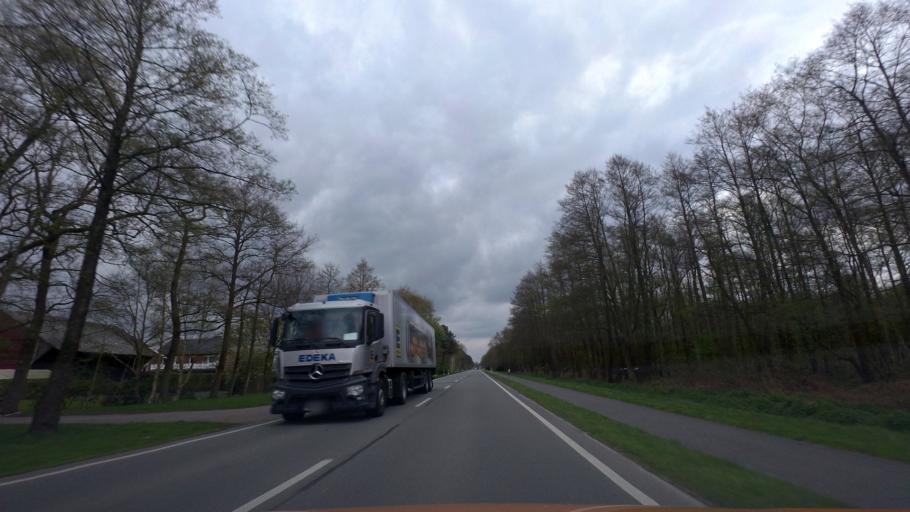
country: DE
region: Lower Saxony
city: Edewecht
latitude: 53.0787
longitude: 7.9321
